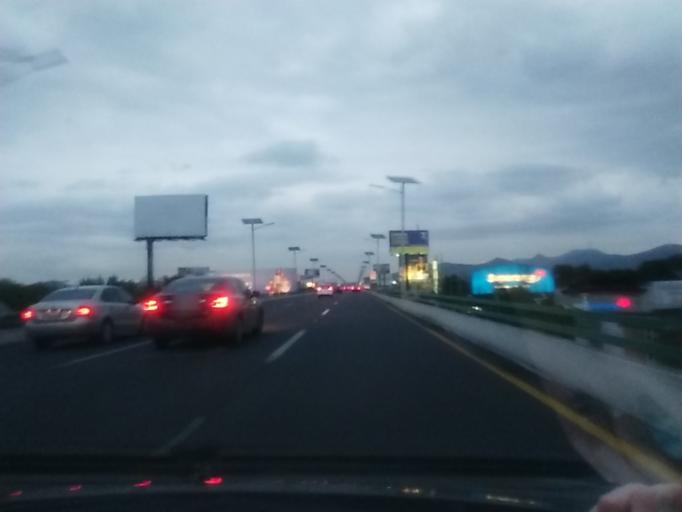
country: MX
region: Mexico
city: Vista Hermosa
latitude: 19.5307
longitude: -99.2213
